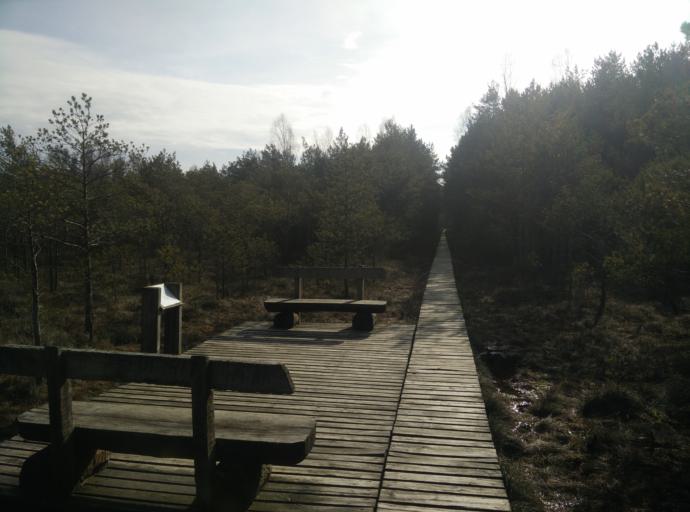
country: LT
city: Trakai
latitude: 54.6422
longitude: 24.9682
